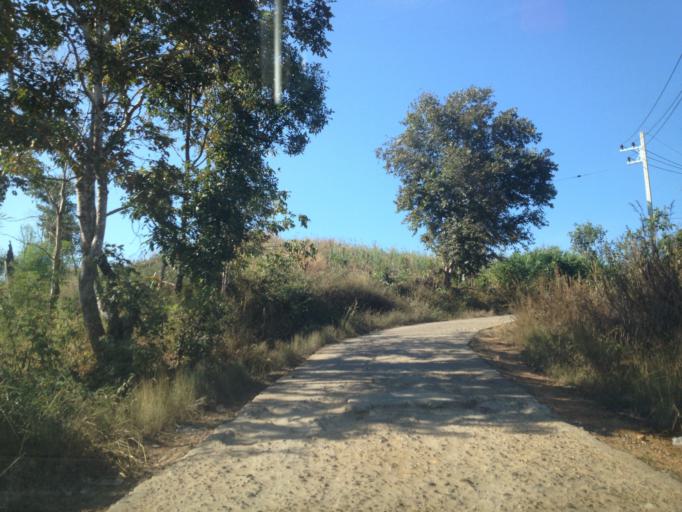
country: TH
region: Mae Hong Son
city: Ban Huai I Huak
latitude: 18.0598
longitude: 98.1785
